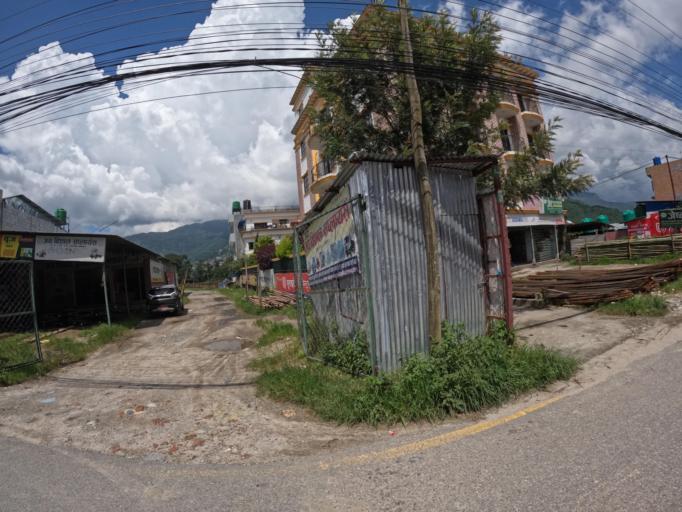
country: NP
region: Central Region
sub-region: Bagmati Zone
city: Kathmandu
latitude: 27.7774
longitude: 85.3264
